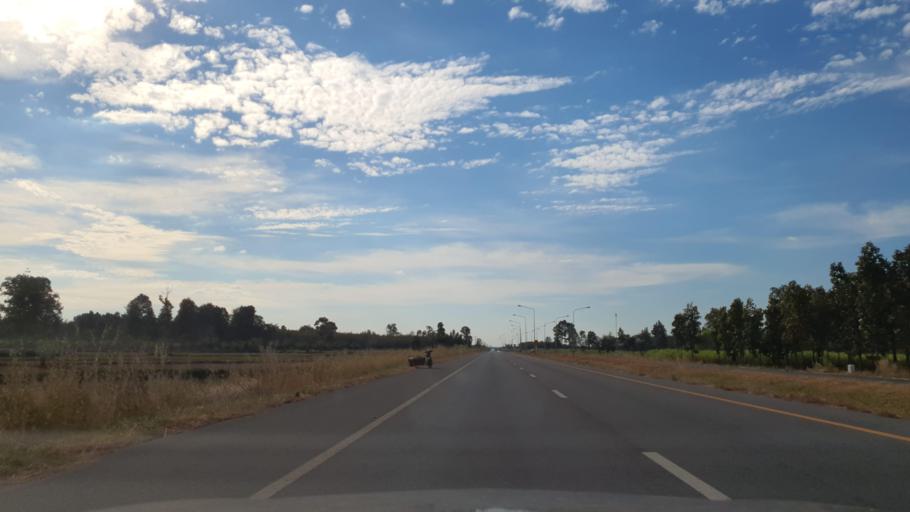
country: TH
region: Roi Et
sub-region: Amphoe Pho Chai
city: Pho Chai
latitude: 16.4154
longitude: 103.8132
